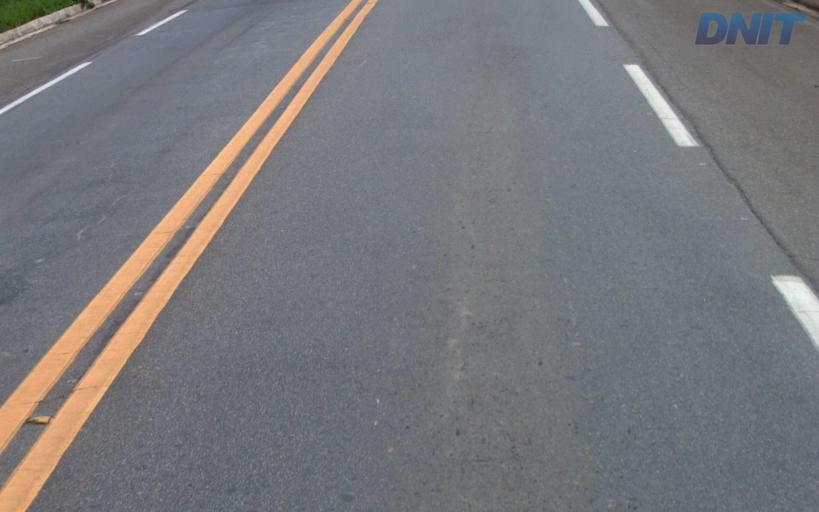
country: BR
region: Minas Gerais
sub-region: Belo Oriente
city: Belo Oriente
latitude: -19.1483
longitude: -42.2321
